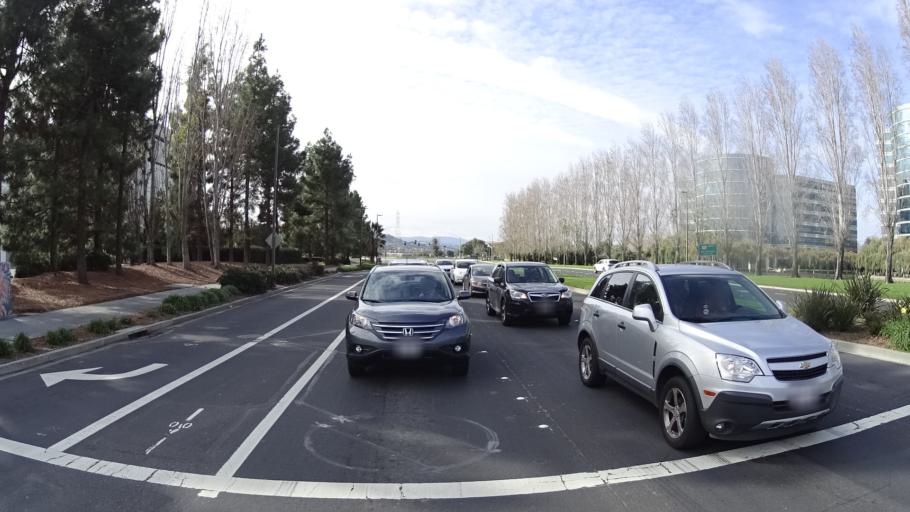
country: US
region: California
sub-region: San Mateo County
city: Belmont
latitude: 37.5284
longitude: -122.2640
